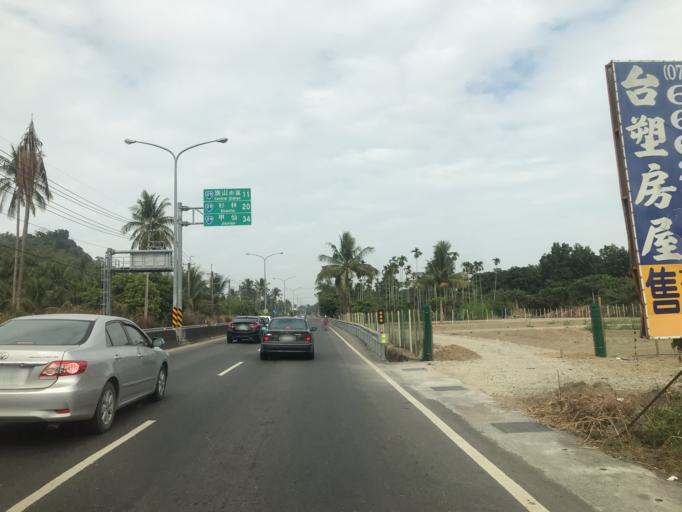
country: TW
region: Taiwan
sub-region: Pingtung
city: Pingtung
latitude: 22.8003
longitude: 120.4593
